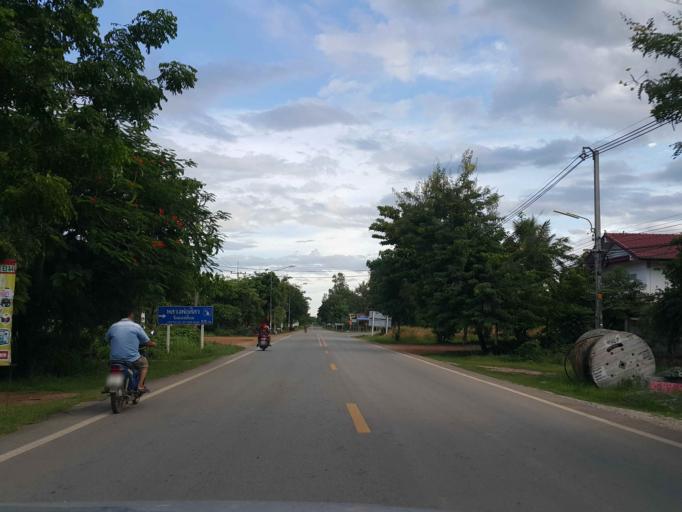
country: TH
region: Sukhothai
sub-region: Amphoe Si Satchanalai
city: Si Satchanalai
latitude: 17.4989
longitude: 99.7526
